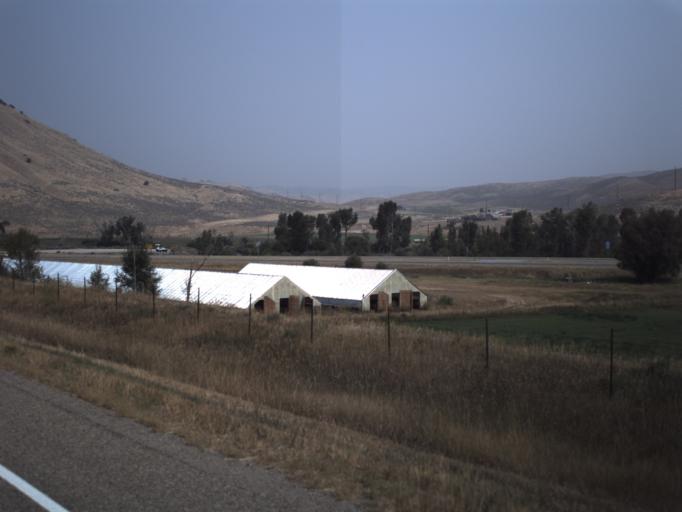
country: US
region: Utah
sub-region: Morgan County
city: Morgan
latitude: 41.0379
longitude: -111.5169
